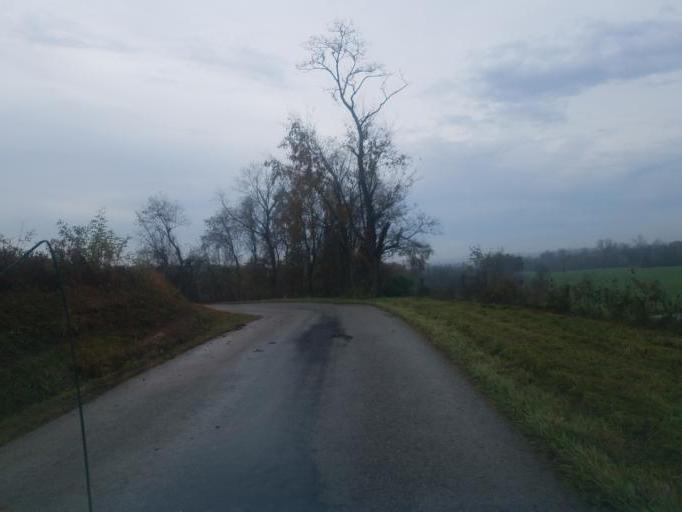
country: US
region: Ohio
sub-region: Morgan County
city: McConnelsville
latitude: 39.5126
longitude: -81.8312
